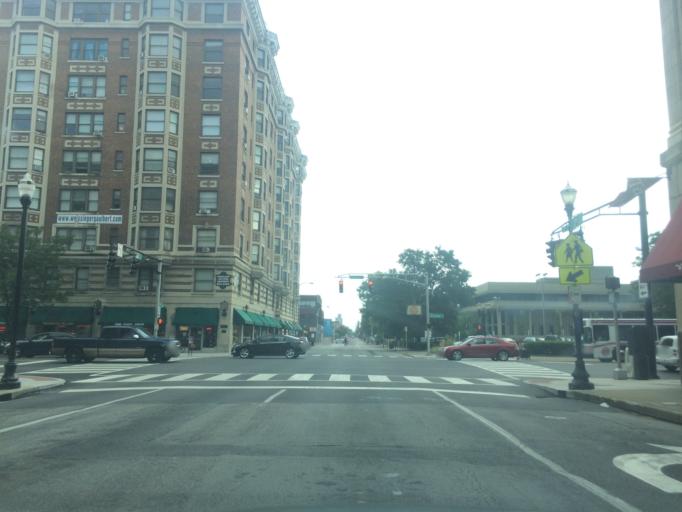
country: US
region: Kentucky
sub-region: Jefferson County
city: Louisville
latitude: 38.2463
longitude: -85.7567
